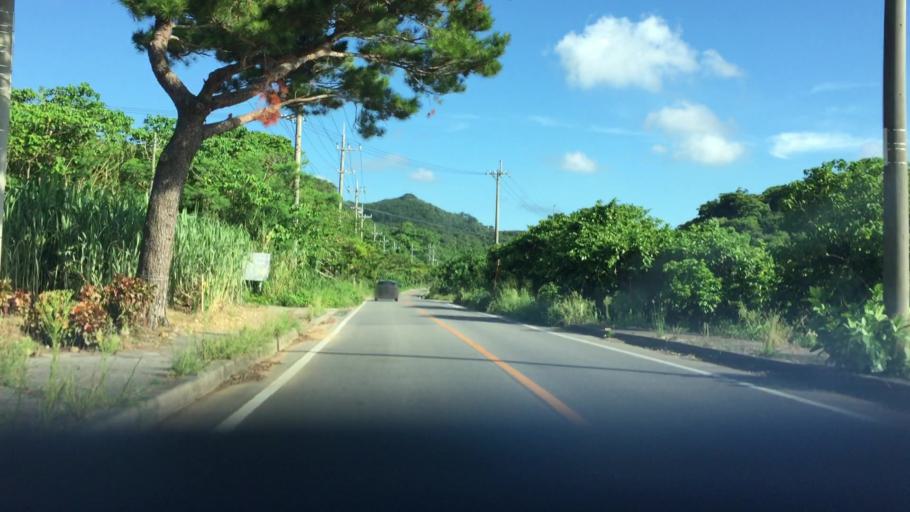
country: JP
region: Okinawa
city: Ishigaki
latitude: 24.3854
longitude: 124.1519
